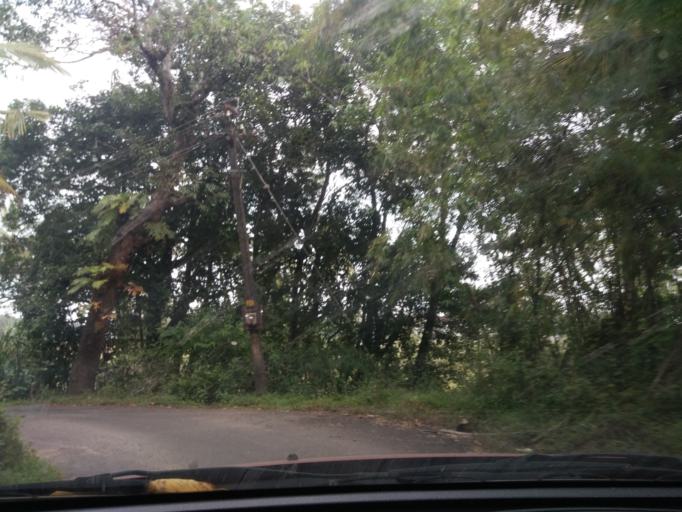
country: IN
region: Goa
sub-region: South Goa
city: Varca
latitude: 15.2238
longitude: 73.9543
